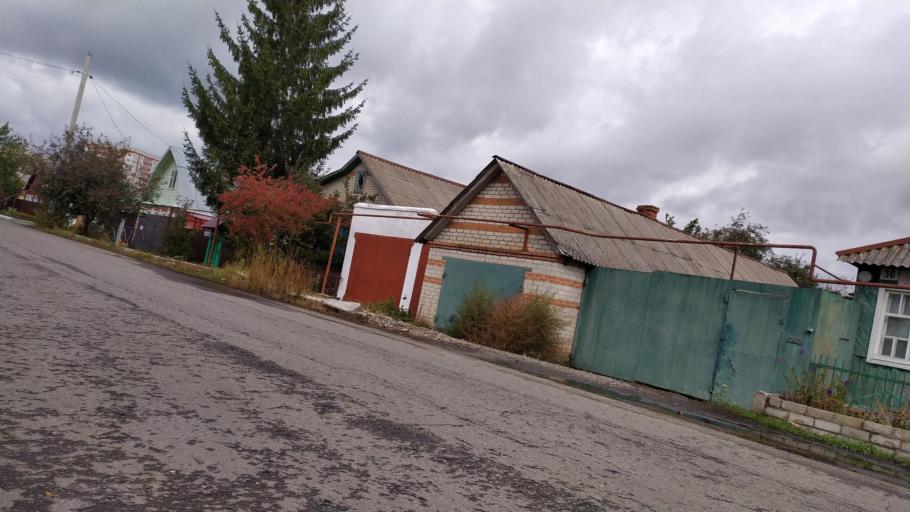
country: RU
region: Kursk
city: Kursk
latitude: 51.6447
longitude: 36.1476
